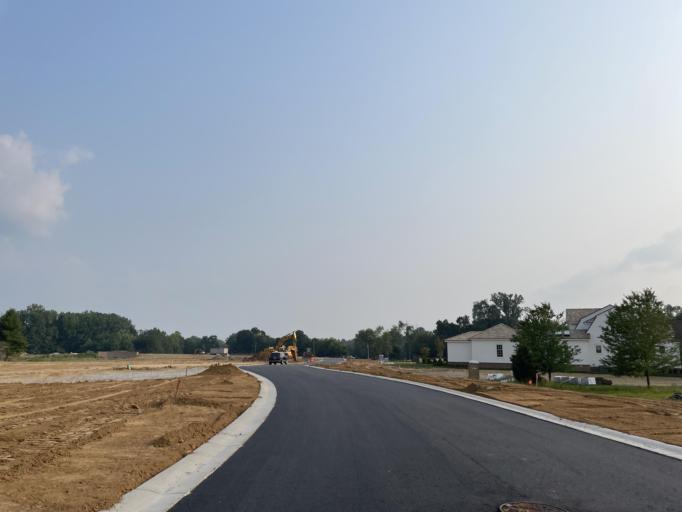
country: US
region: Kentucky
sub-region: Jefferson County
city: Prospect
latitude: 38.3588
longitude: -85.6259
